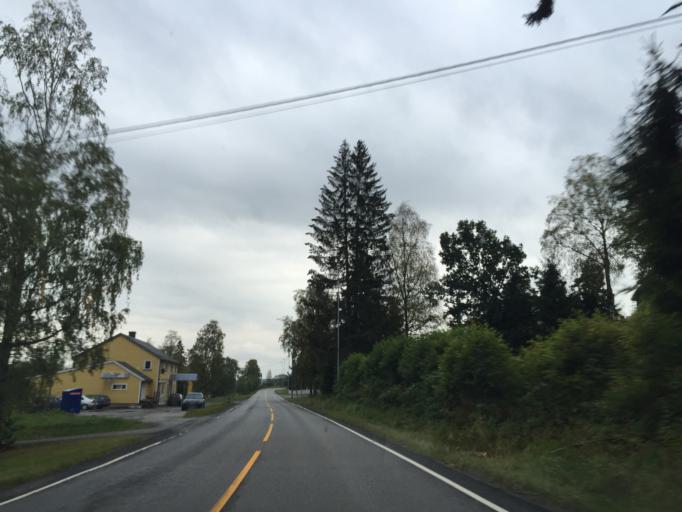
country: NO
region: Hedmark
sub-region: Nord-Odal
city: Sand
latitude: 60.3893
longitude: 11.5393
